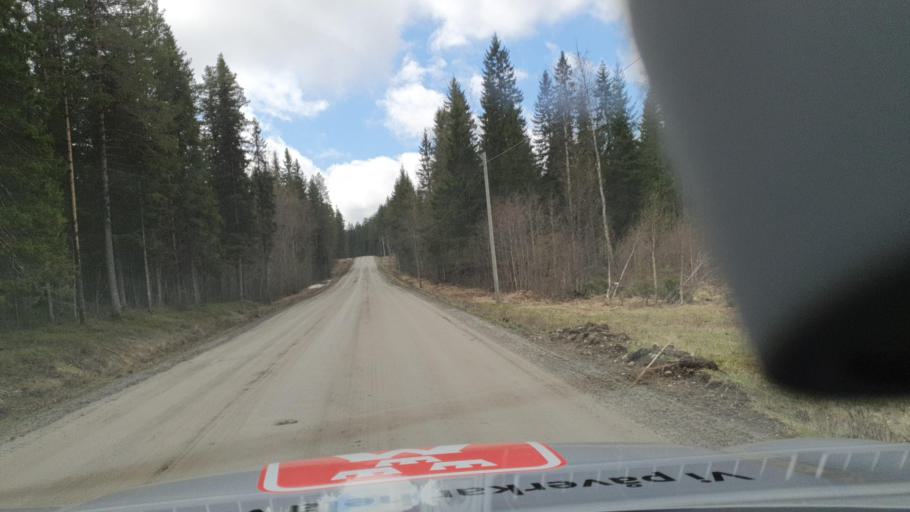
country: SE
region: Vaesterbotten
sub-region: Bjurholms Kommun
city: Bjurholm
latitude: 63.7040
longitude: 18.9023
